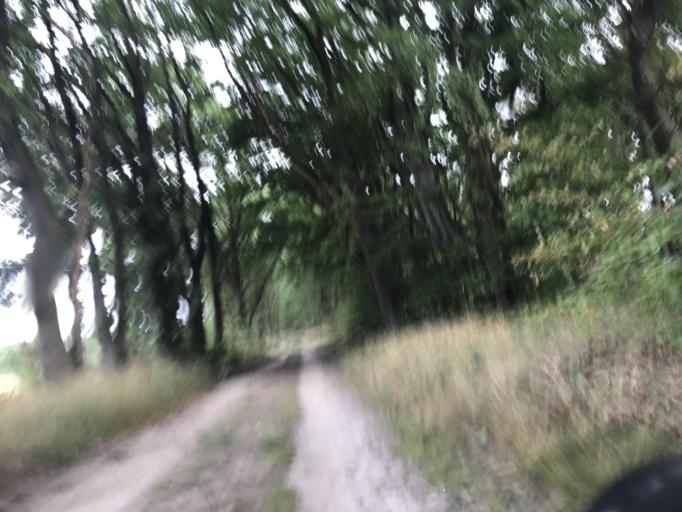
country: DE
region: Lower Saxony
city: Barendorf
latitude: 53.2226
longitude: 10.5304
